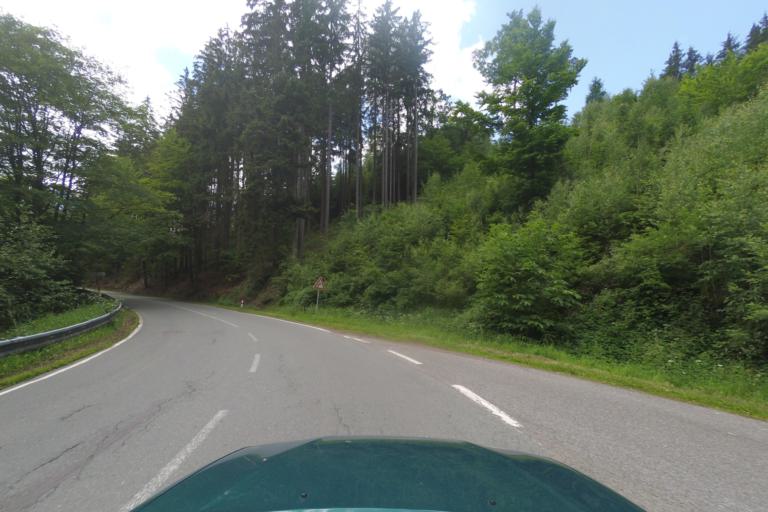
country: PL
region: Lower Silesian Voivodeship
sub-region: Powiat klodzki
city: Lewin Klodzki
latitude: 50.3484
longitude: 16.2400
